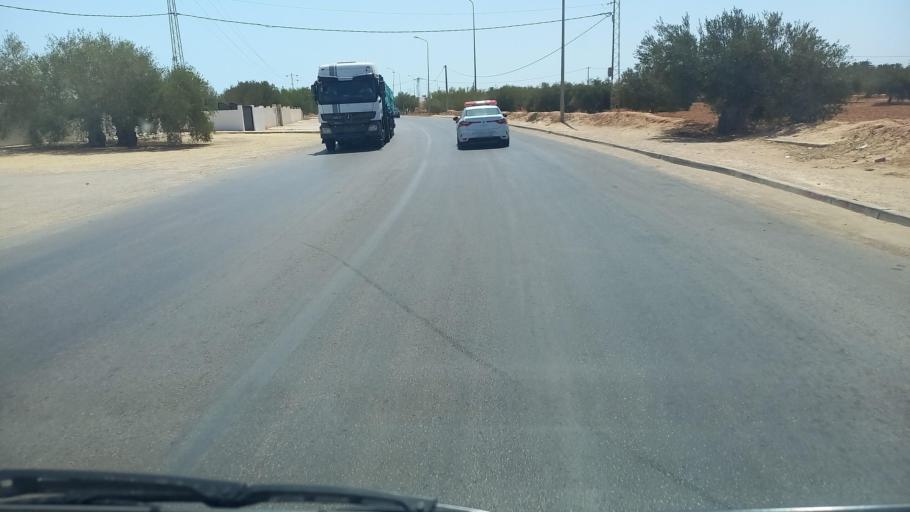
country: TN
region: Madanin
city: Houmt Souk
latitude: 33.7814
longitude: 10.8893
